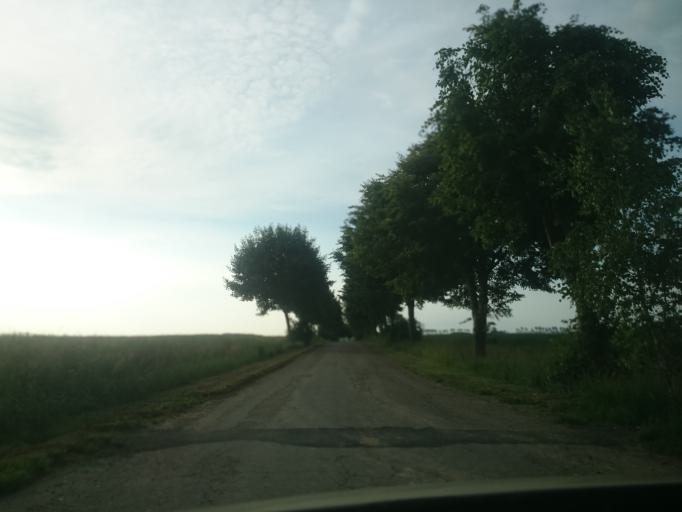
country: DE
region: Saxony
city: Eppendorf
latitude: 50.8348
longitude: 13.2288
